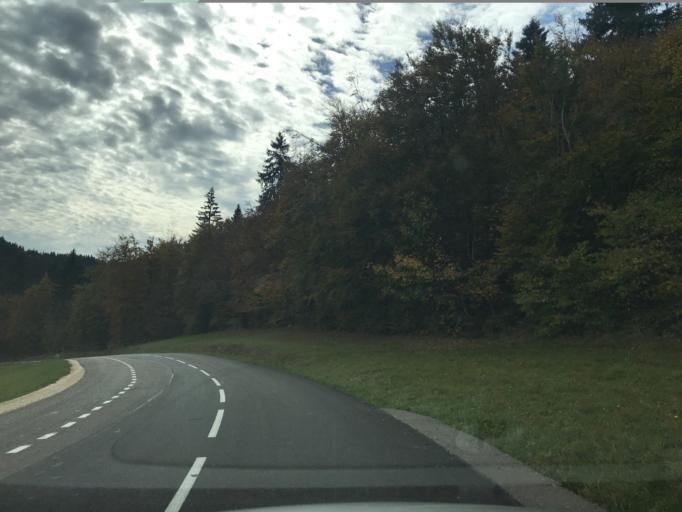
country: FR
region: Rhone-Alpes
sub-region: Departement de la Savoie
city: Vimines
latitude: 45.4576
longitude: 5.8576
